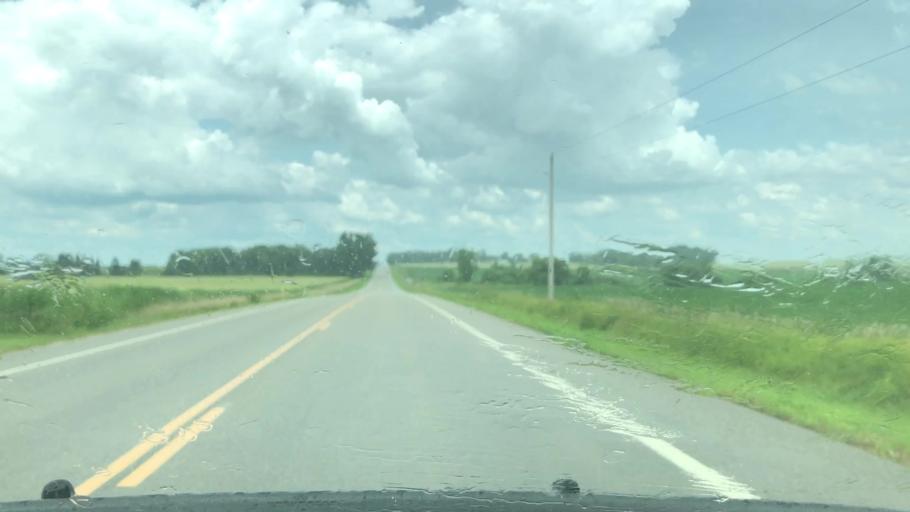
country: US
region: Minnesota
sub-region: Olmsted County
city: Stewartville
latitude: 43.8751
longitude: -92.5286
